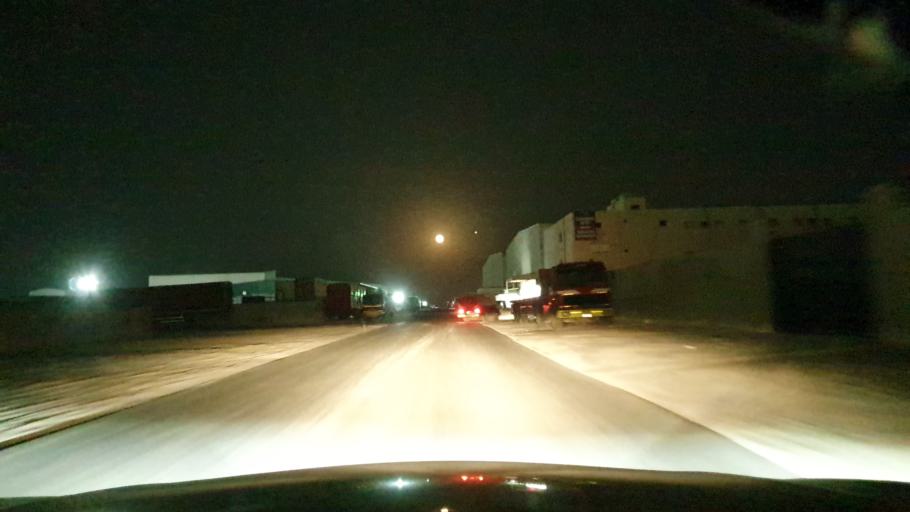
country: BH
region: Northern
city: Sitrah
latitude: 26.0973
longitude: 50.6184
